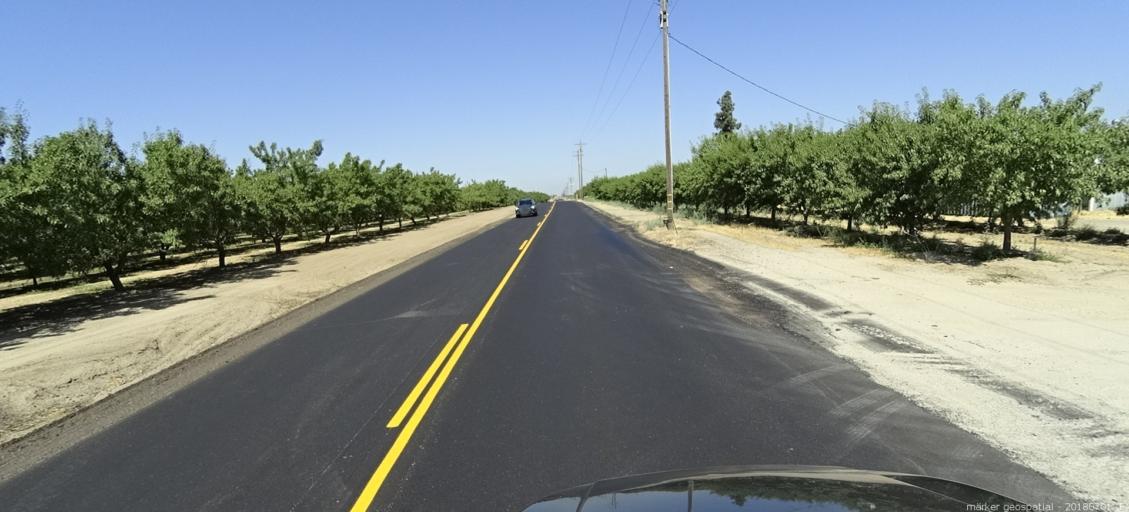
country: US
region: California
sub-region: Madera County
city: Parksdale
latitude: 36.8803
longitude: -119.9504
